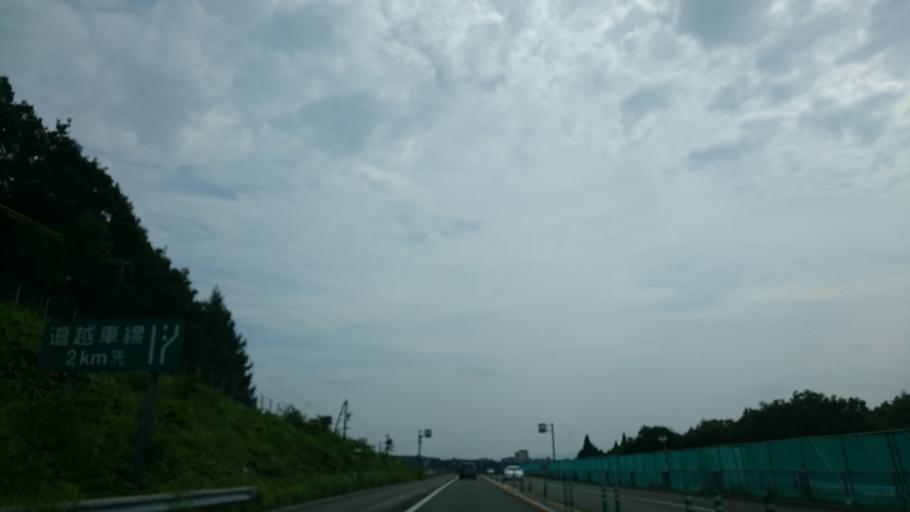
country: JP
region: Gifu
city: Gujo
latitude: 36.0064
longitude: 136.9287
